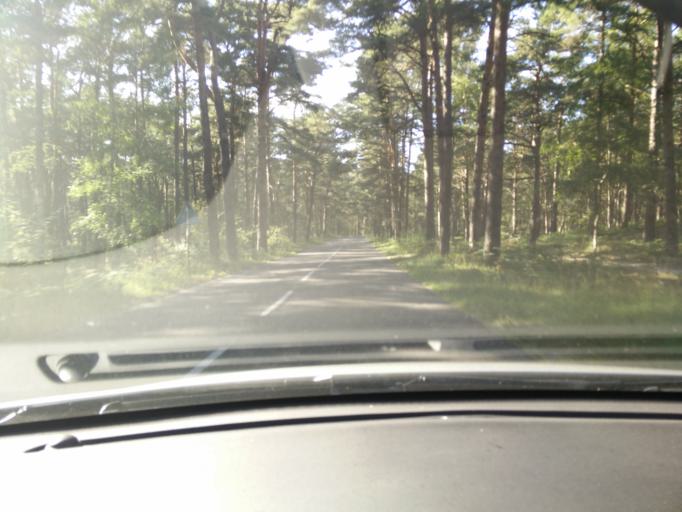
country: PL
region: Pomeranian Voivodeship
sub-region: Powiat pucki
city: Hel
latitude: 54.6389
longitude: 18.7755
